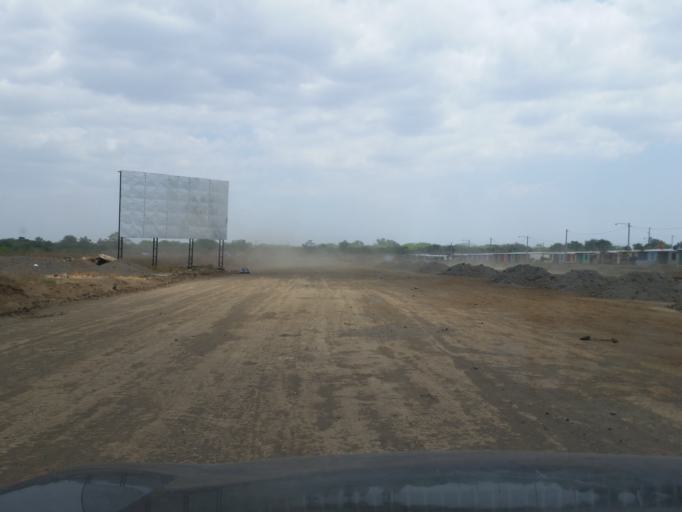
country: NI
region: Managua
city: Tipitapa
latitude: 12.1345
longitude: -86.1580
